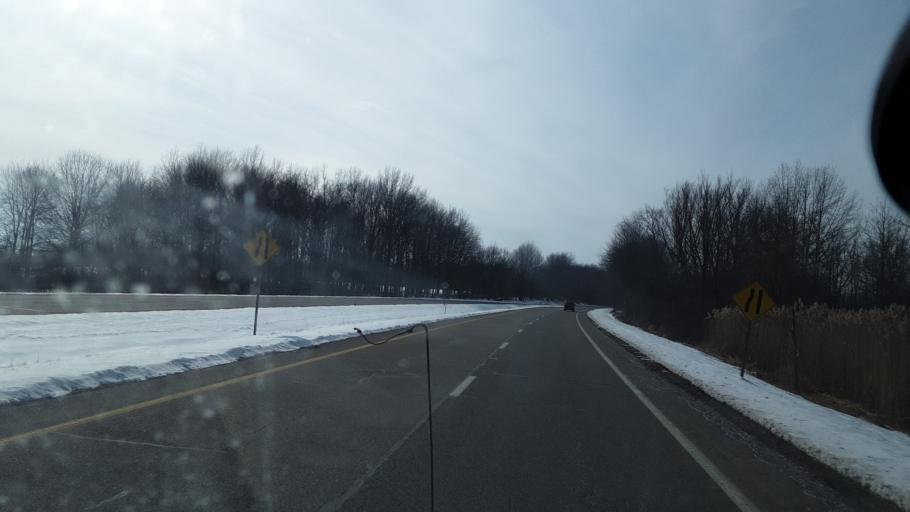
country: US
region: Ohio
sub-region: Portage County
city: Ravenna
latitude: 41.0304
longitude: -81.2177
